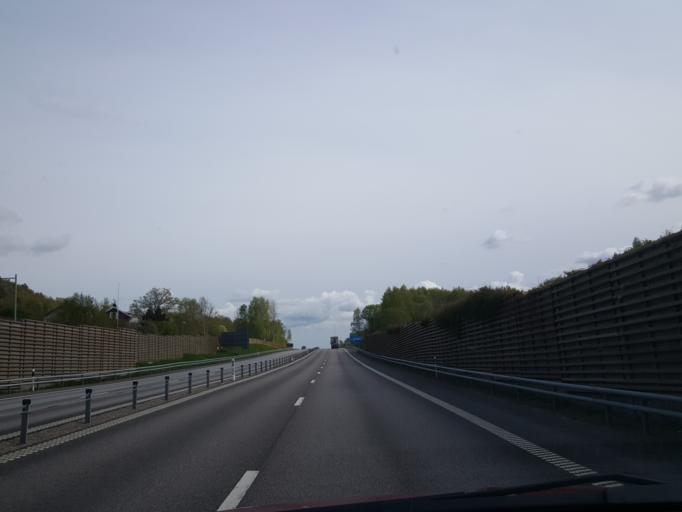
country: SE
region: Vaestra Goetaland
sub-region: Lilla Edets Kommun
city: Lilla Edet
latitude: 58.1352
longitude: 12.1358
